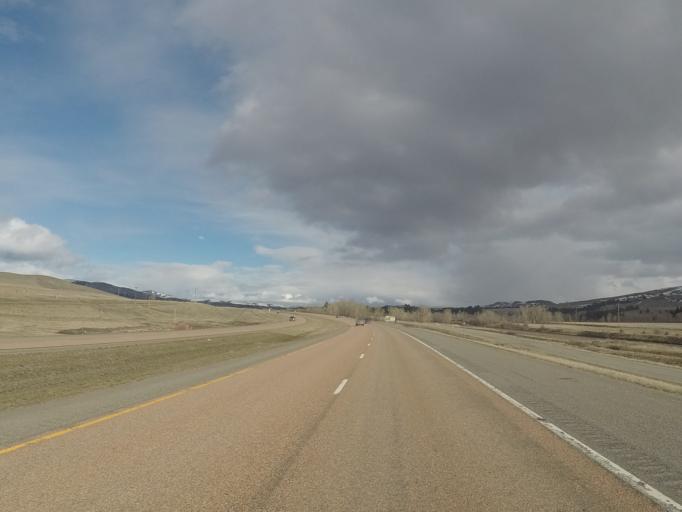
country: US
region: Montana
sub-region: Powell County
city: Deer Lodge
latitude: 46.6075
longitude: -113.0210
